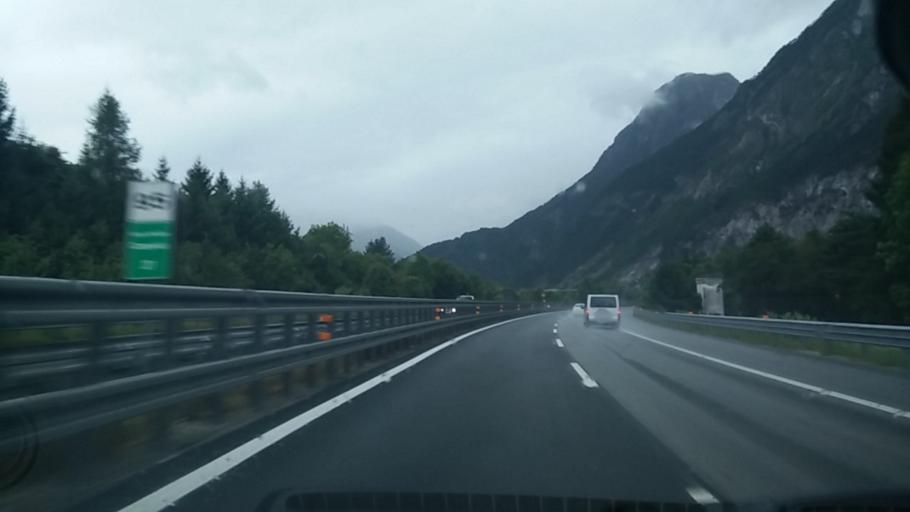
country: IT
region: Friuli Venezia Giulia
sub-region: Provincia di Udine
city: Pontebba
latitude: 46.5069
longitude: 13.3568
